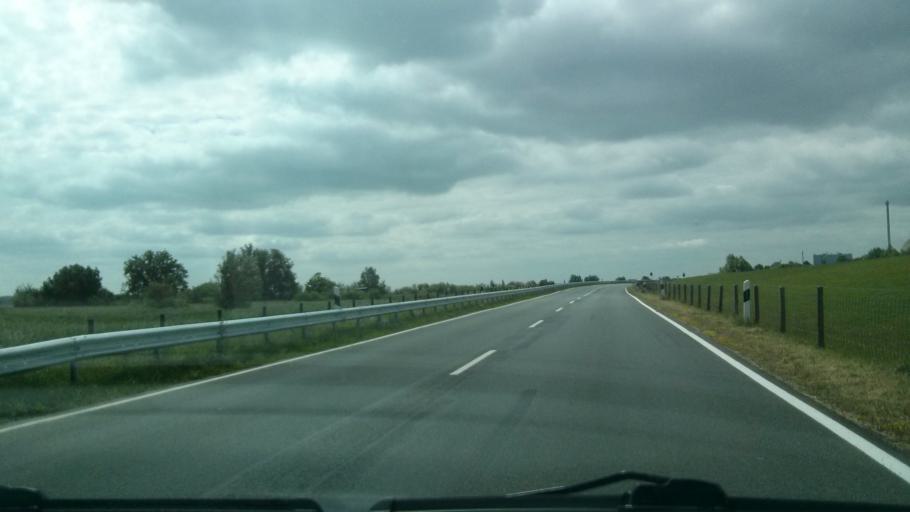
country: DE
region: Lower Saxony
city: Nordenham
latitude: 53.4391
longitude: 8.4797
